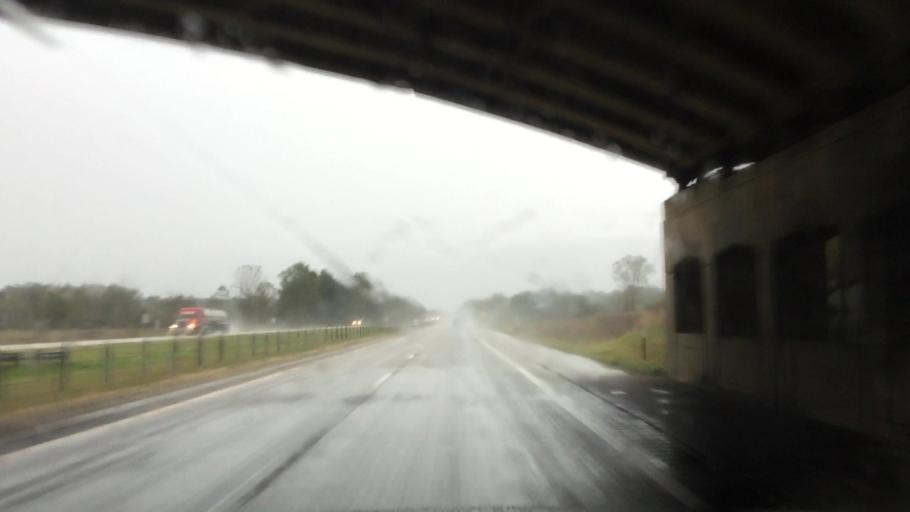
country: US
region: Michigan
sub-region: Van Buren County
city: Paw Paw
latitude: 42.2064
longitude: -85.8899
